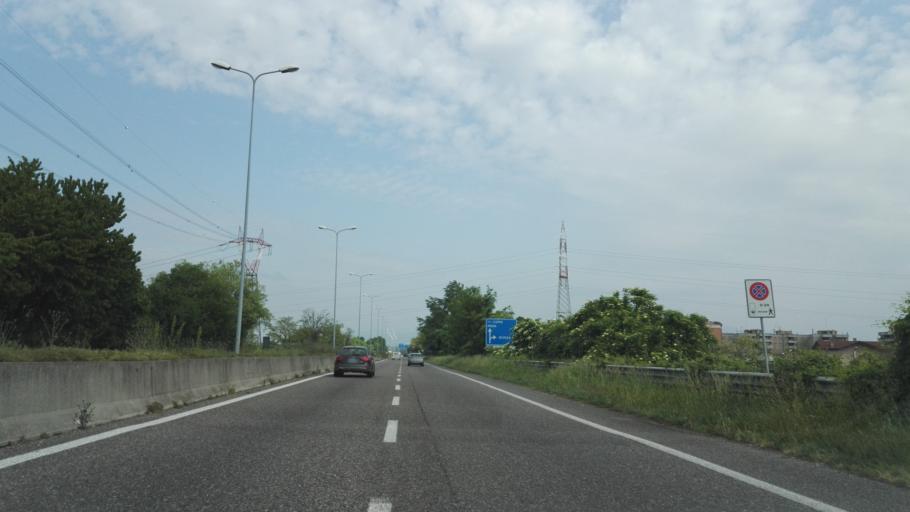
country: IT
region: Lombardy
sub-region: Provincia di Monza e Brianza
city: Cesano Maderno
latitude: 45.6319
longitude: 9.1618
